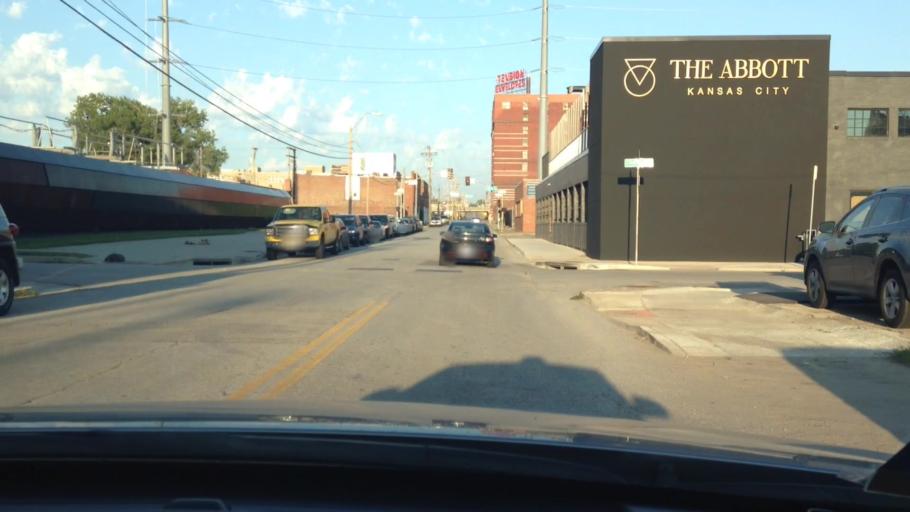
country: US
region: Missouri
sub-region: Jackson County
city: Kansas City
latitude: 39.0902
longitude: -94.5770
